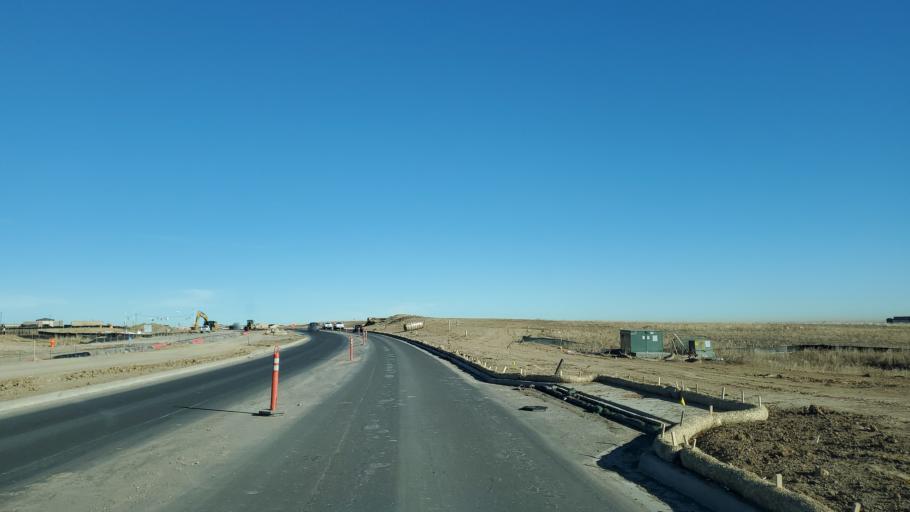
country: US
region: Colorado
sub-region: Boulder County
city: Erie
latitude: 39.9961
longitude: -105.0089
